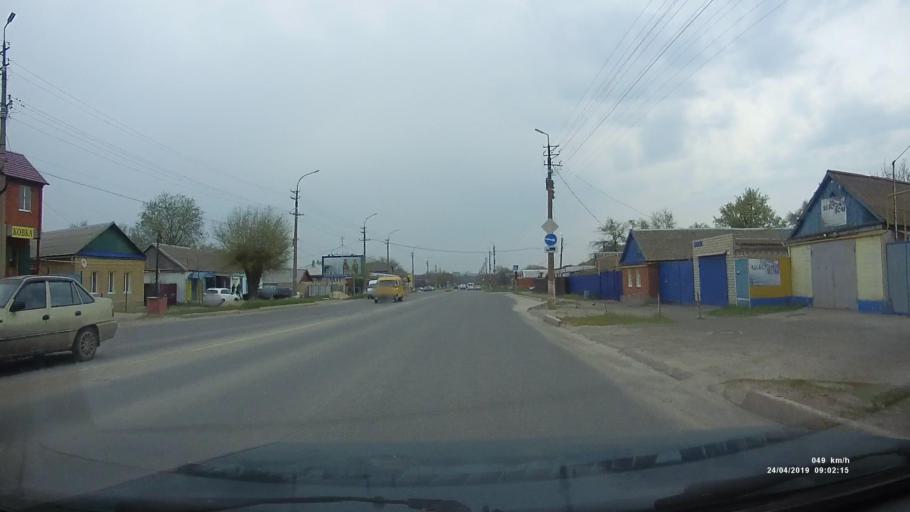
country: RU
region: Kalmykiya
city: Elista
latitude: 46.3120
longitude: 44.2325
